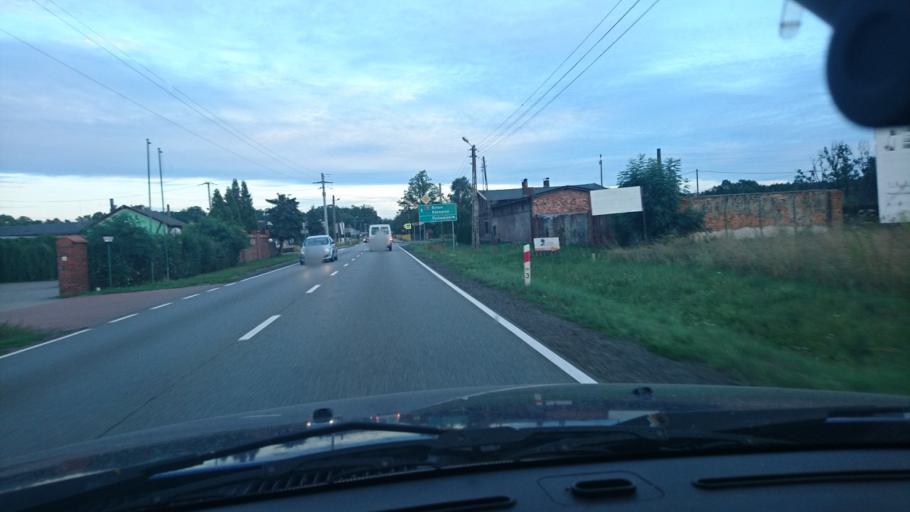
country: PL
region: Silesian Voivodeship
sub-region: Powiat tarnogorski
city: Tworog
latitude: 50.5175
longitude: 18.7305
